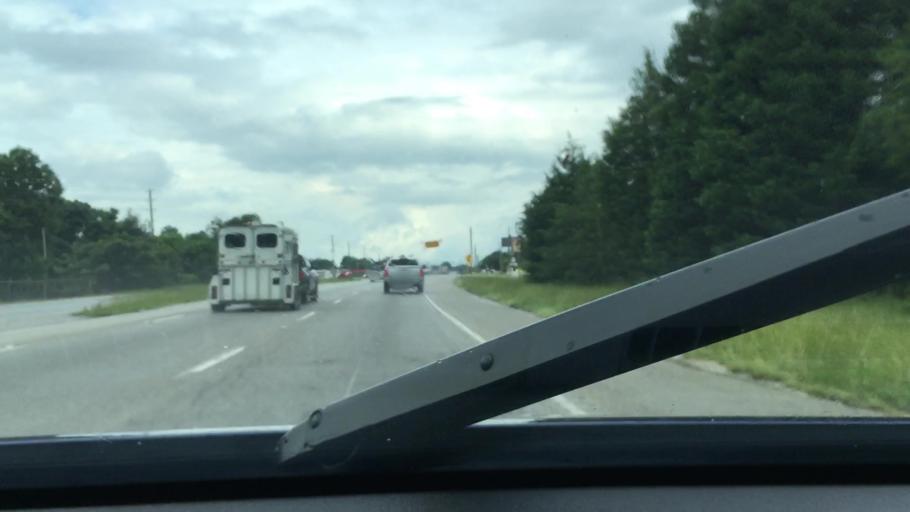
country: US
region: South Carolina
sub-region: Sumter County
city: Cherryvale
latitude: 33.9641
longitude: -80.4172
